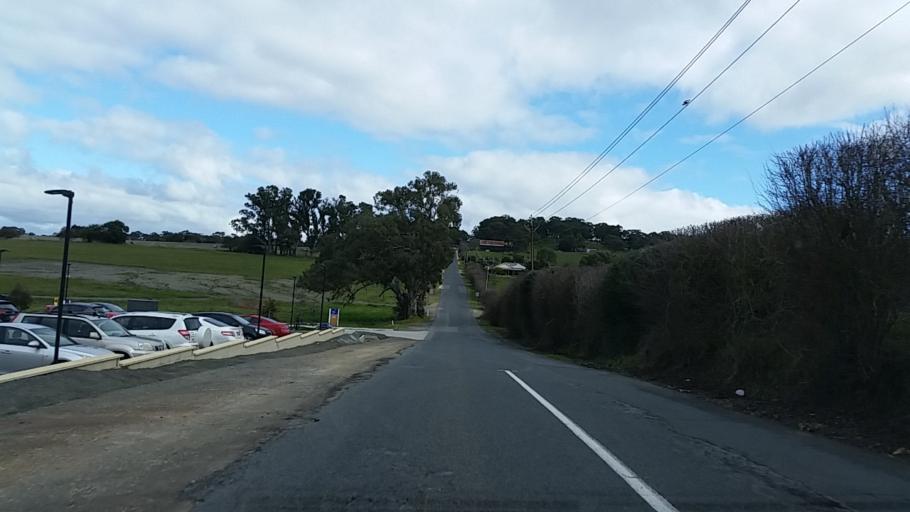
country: AU
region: South Australia
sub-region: Mount Barker
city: Little Hampton
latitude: -35.0655
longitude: 138.8504
